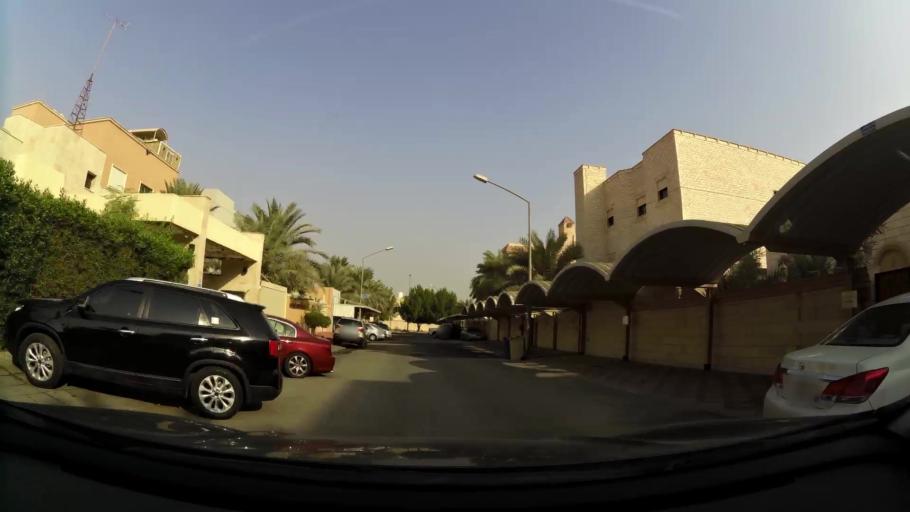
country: KW
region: Mubarak al Kabir
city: Sabah as Salim
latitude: 29.2712
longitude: 48.0741
